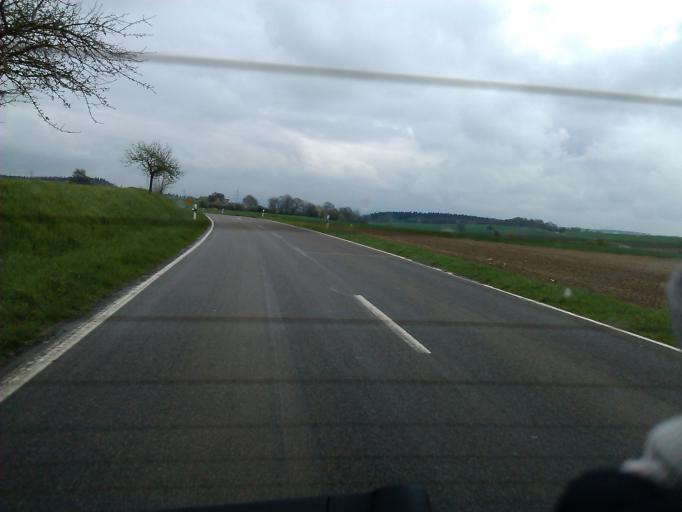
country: DE
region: Baden-Wuerttemberg
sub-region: Regierungsbezirk Stuttgart
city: Siegelsbach
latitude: 49.2655
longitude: 9.0840
